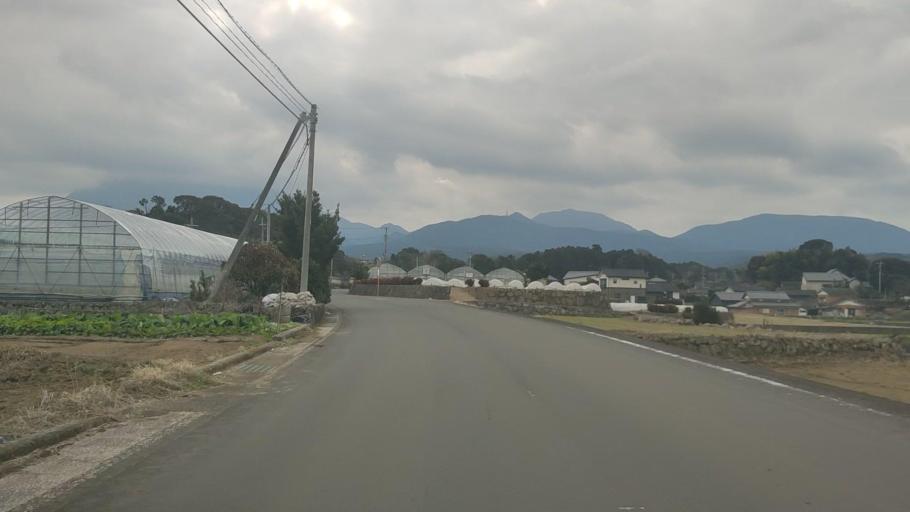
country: JP
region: Nagasaki
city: Shimabara
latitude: 32.8395
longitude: 130.2954
